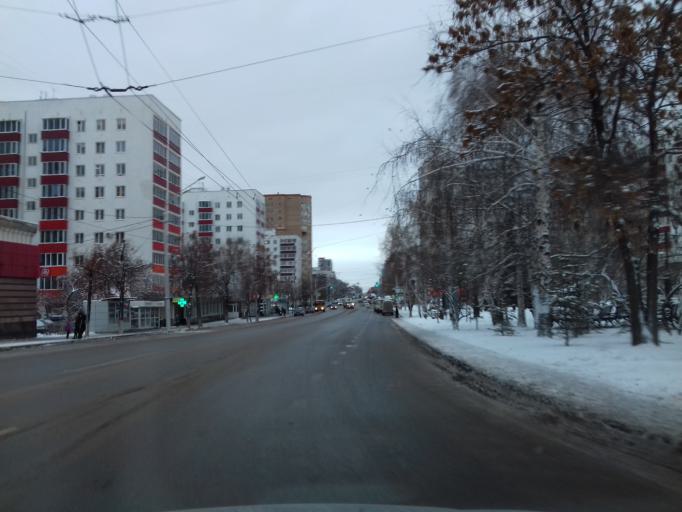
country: RU
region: Bashkortostan
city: Ufa
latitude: 54.7231
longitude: 55.9270
